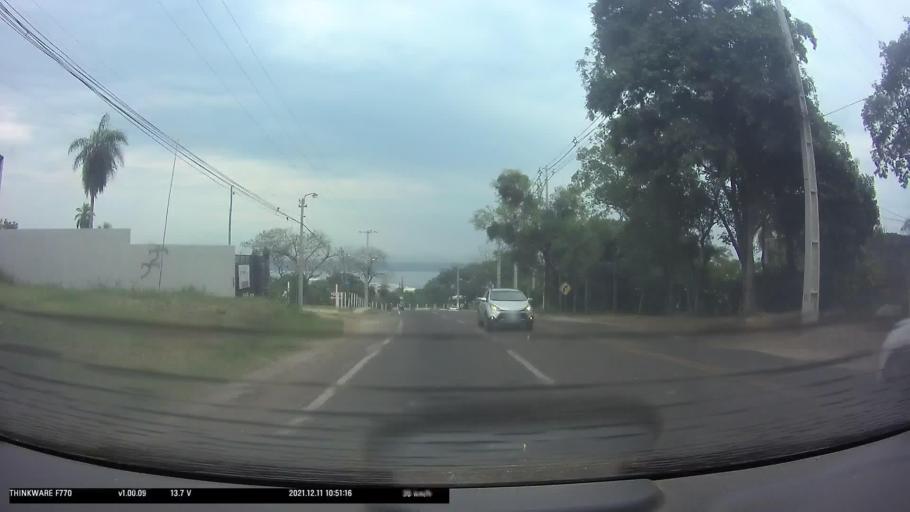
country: PY
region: Cordillera
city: San Bernardino
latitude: -25.2983
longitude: -57.2712
